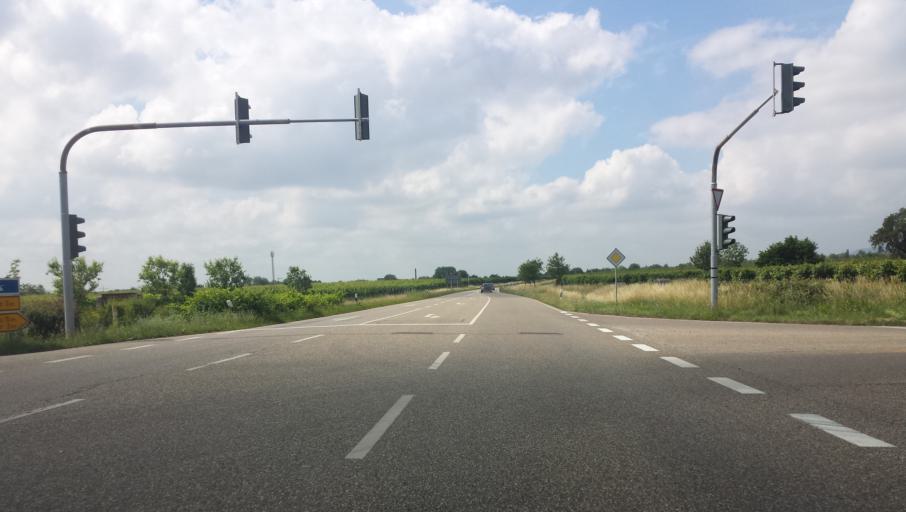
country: DE
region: Rheinland-Pfalz
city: Maikammer
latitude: 49.3194
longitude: 8.1488
